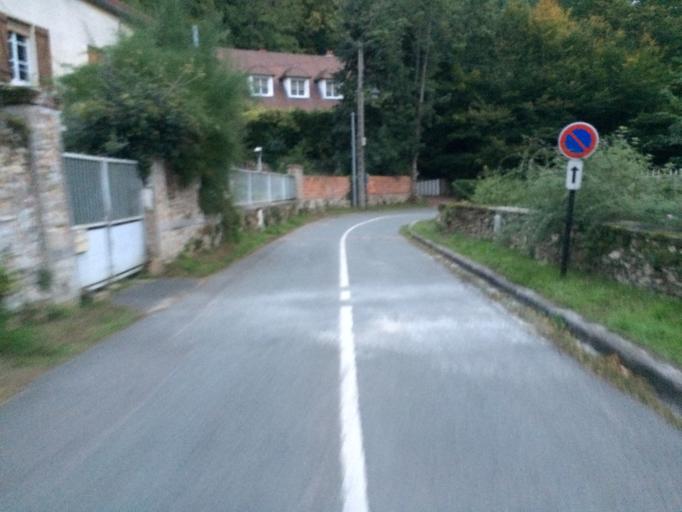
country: FR
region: Ile-de-France
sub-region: Departement de l'Essonne
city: Bievres
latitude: 48.7596
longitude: 2.1981
